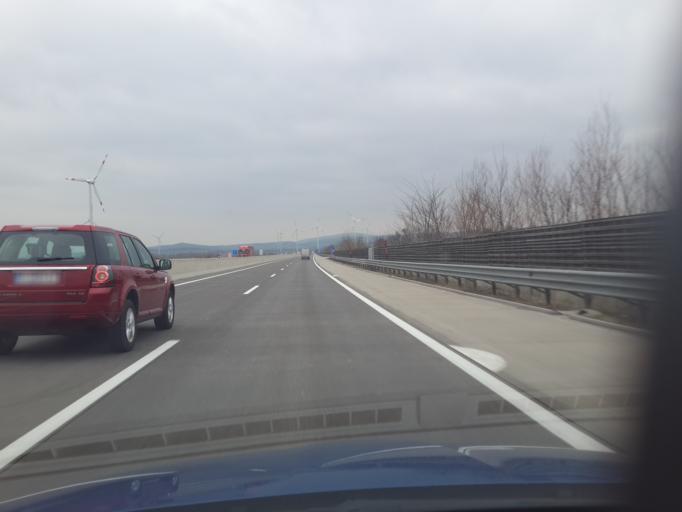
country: AT
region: Burgenland
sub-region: Politischer Bezirk Neusiedl am See
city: Kittsee
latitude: 48.0762
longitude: 17.0567
